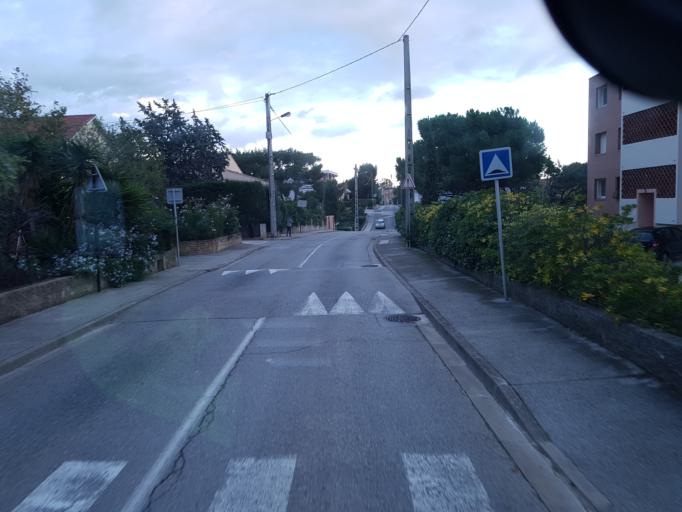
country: FR
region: Provence-Alpes-Cote d'Azur
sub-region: Departement du Var
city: Bandol
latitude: 43.1406
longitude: 5.7447
